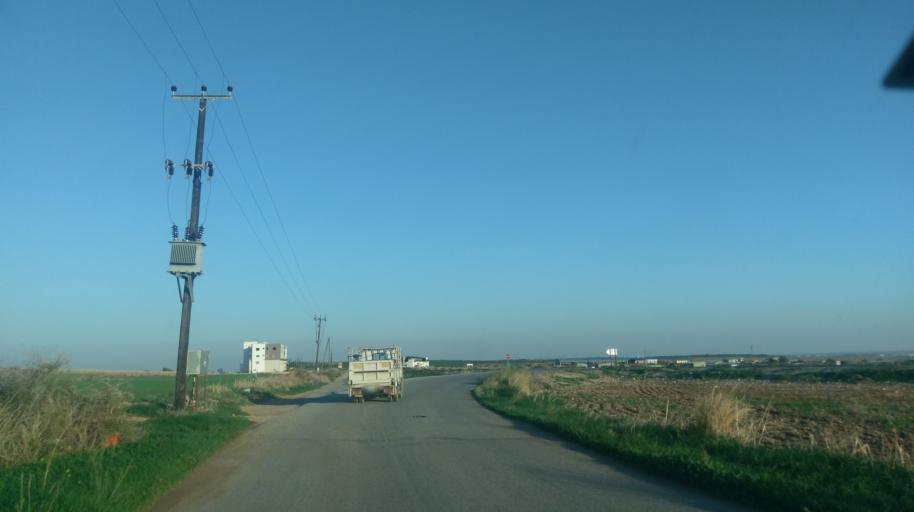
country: CY
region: Ammochostos
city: Lefkonoiko
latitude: 35.2337
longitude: 33.5616
